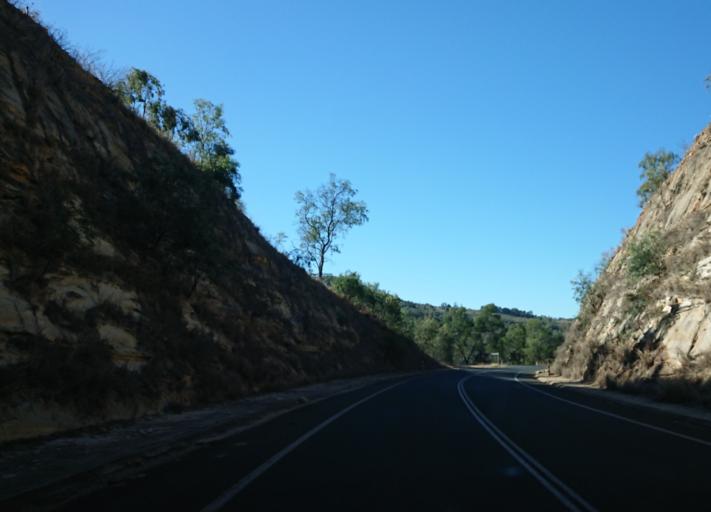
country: AU
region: Queensland
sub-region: Toowoomba
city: Rangeville
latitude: -27.7217
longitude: 152.1162
